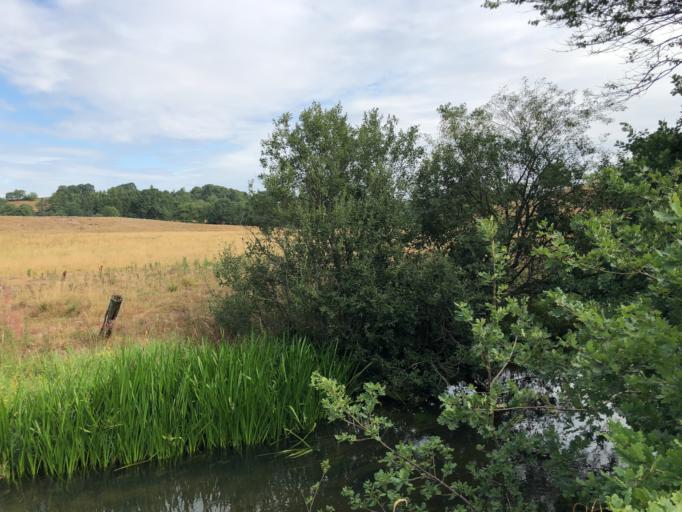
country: DK
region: South Denmark
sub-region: Vejle Kommune
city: Egtved
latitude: 55.6515
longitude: 9.2837
